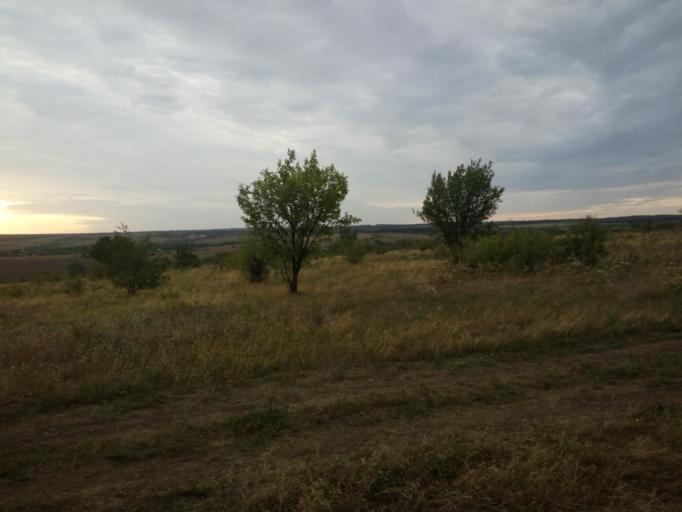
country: RU
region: Rostov
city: Gornyy
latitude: 47.8891
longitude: 40.2409
